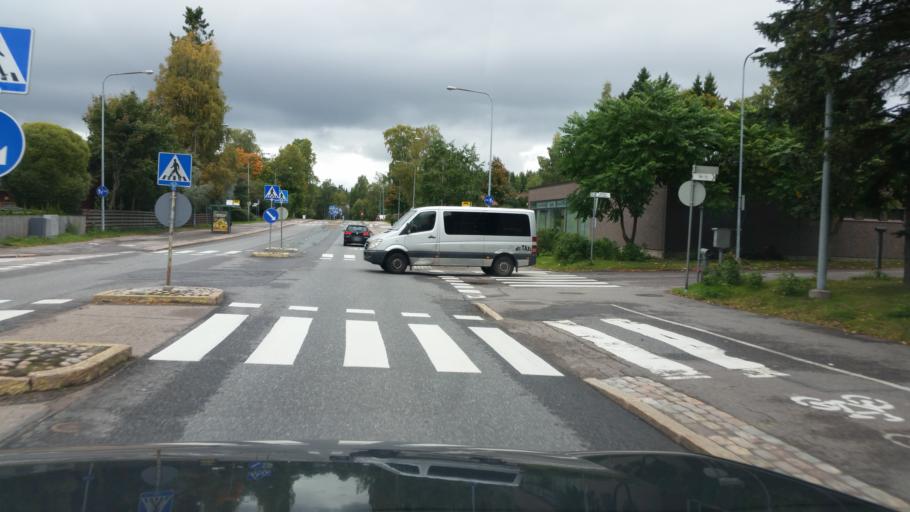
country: FI
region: Uusimaa
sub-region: Helsinki
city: Helsinki
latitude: 60.2438
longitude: 24.9256
